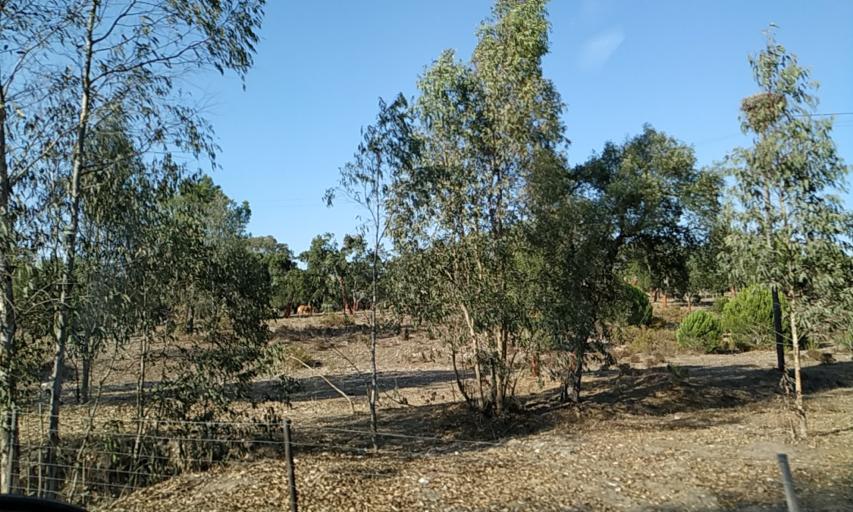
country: PT
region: Santarem
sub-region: Almeirim
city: Fazendas de Almeirim
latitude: 39.1328
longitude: -8.6087
